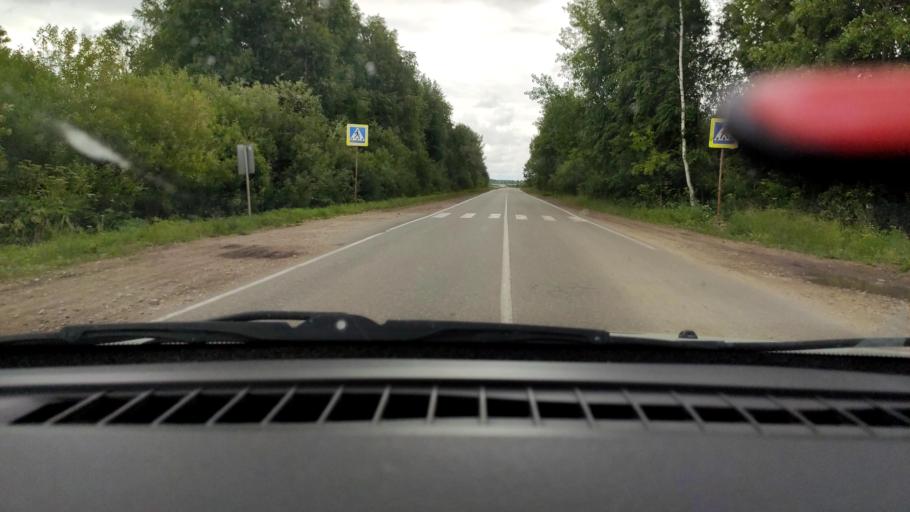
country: RU
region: Perm
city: Chaykovskaya
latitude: 58.0877
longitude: 55.6126
